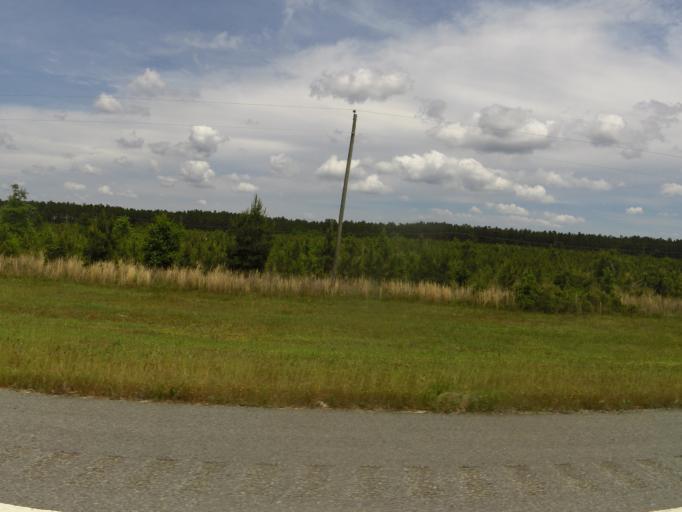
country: US
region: Georgia
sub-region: Jefferson County
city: Wadley
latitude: 32.8022
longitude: -82.4000
